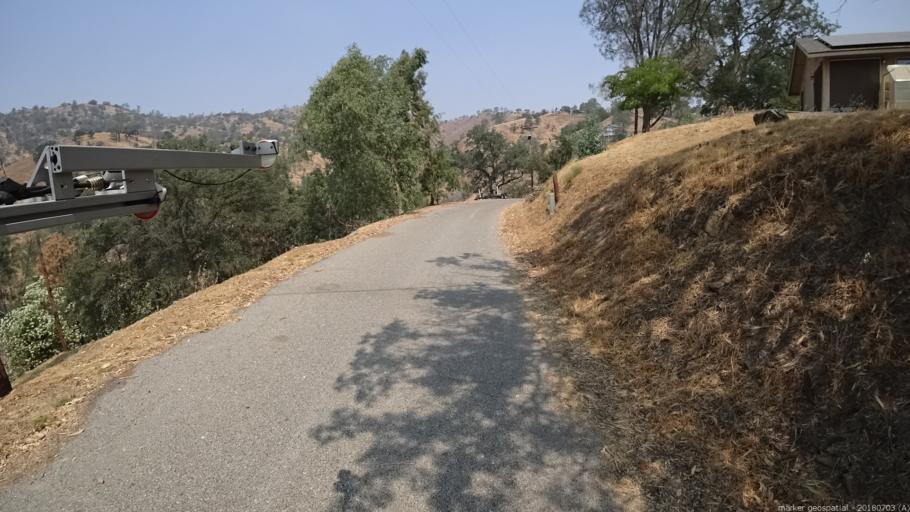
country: US
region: California
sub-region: Fresno County
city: Auberry
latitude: 37.0462
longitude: -119.6534
